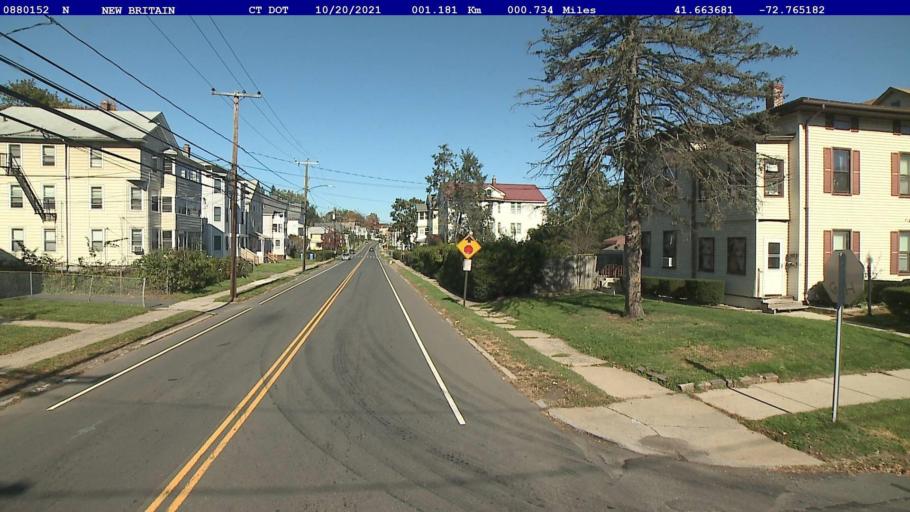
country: US
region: Connecticut
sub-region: Hartford County
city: New Britain
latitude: 41.6637
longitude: -72.7652
